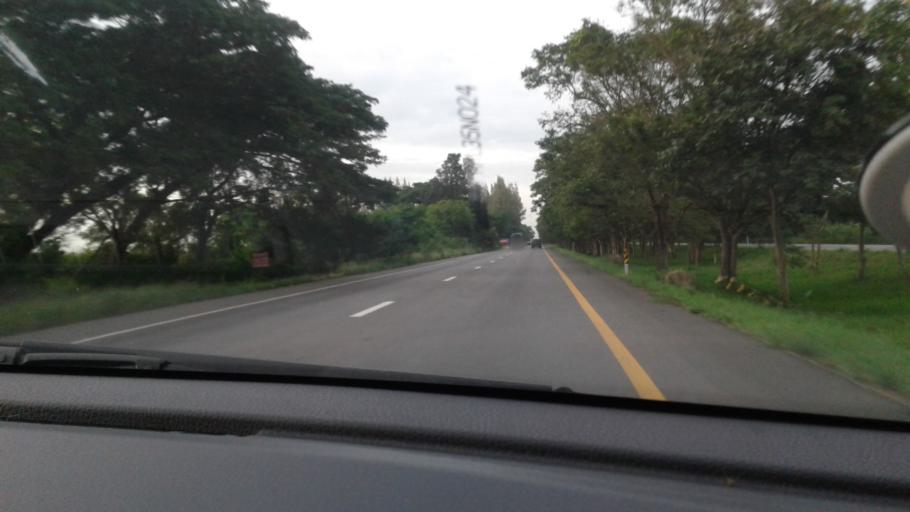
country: TH
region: Prachuap Khiri Khan
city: Pran Buri
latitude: 12.4739
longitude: 99.8944
